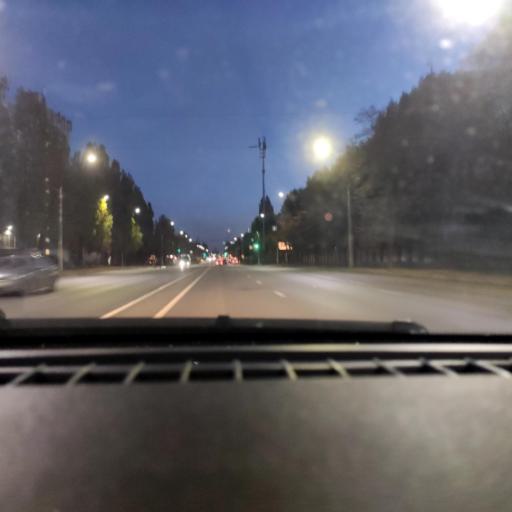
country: RU
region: Voronezj
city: Voronezh
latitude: 51.6779
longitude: 39.2590
